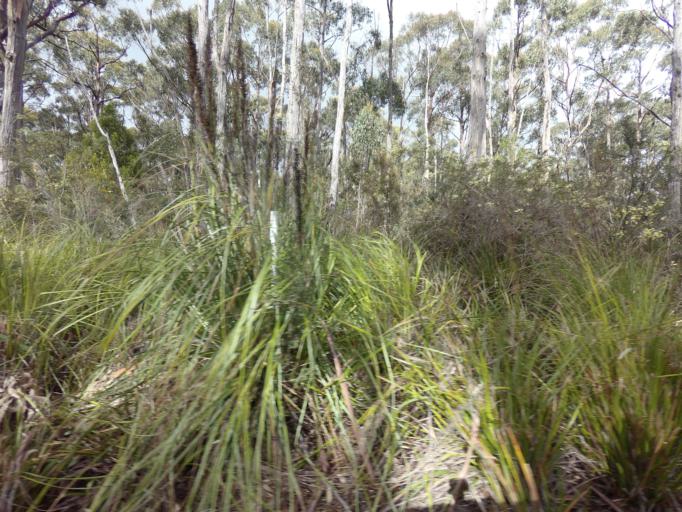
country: AU
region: Tasmania
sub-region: Huon Valley
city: Geeveston
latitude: -43.4614
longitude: 146.9103
